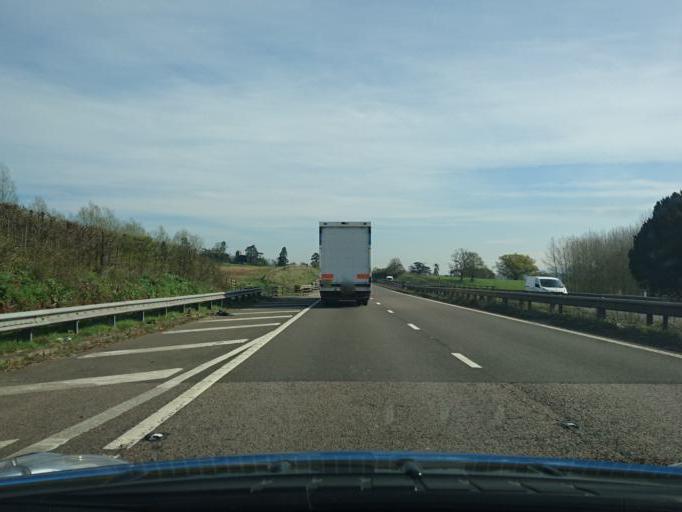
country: GB
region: England
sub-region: Worcestershire
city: Upton upon Severn
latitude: 52.0239
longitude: -2.2095
